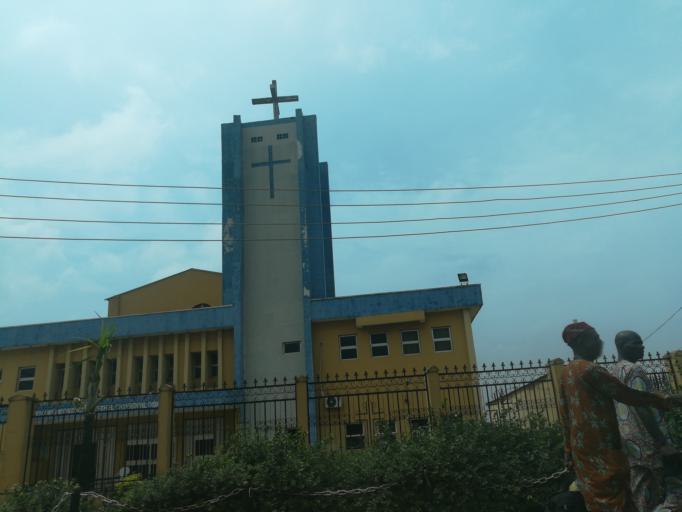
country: NG
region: Lagos
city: Ikorodu
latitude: 6.6103
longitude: 3.5060
